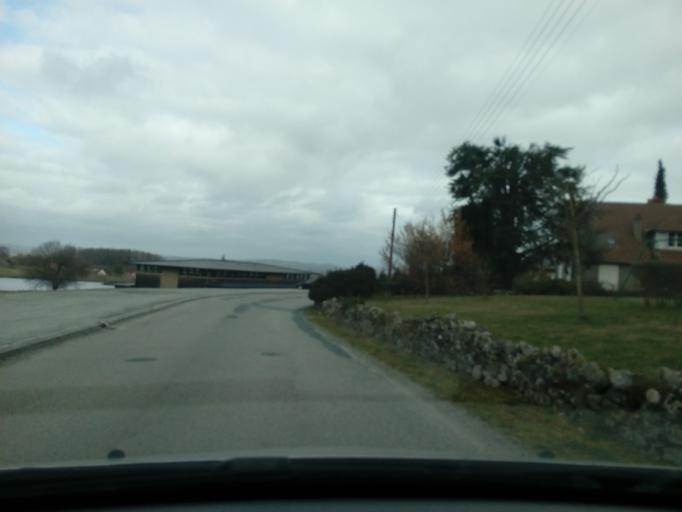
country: FR
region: Limousin
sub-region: Departement de la Creuse
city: Sainte-Feyre
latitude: 46.1395
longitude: 1.9196
